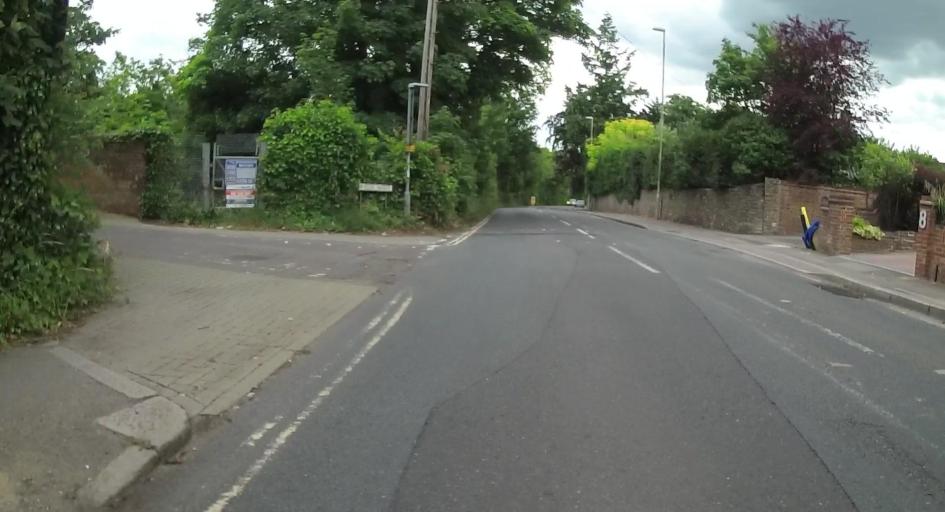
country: GB
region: England
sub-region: Hampshire
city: Aldershot
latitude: 51.2412
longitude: -0.7661
